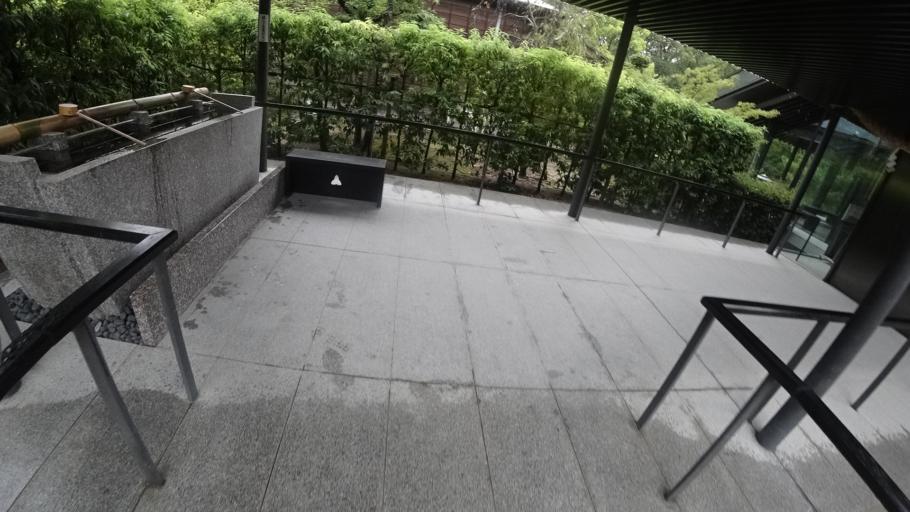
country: JP
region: Hyogo
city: Nishinomiya-hama
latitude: 34.7350
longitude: 135.3349
